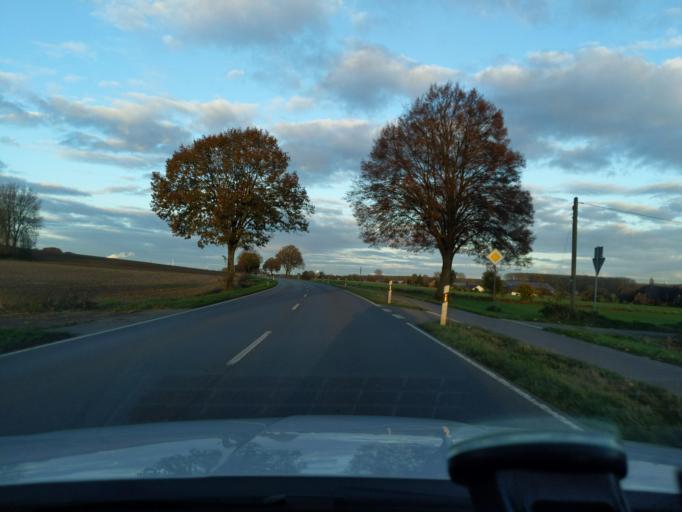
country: DE
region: North Rhine-Westphalia
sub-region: Regierungsbezirk Dusseldorf
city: Uedem
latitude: 51.6745
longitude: 6.3052
